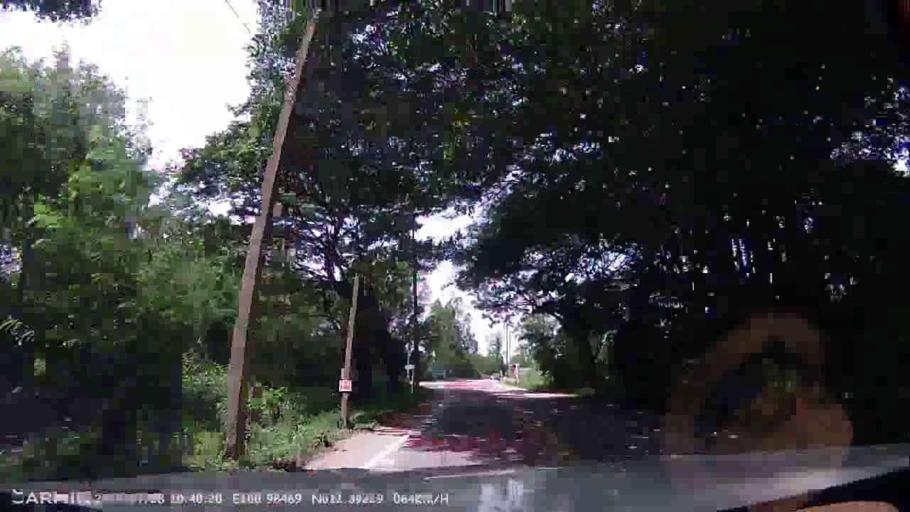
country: TH
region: Chon Buri
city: Phatthaya
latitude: 12.8922
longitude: 100.9847
